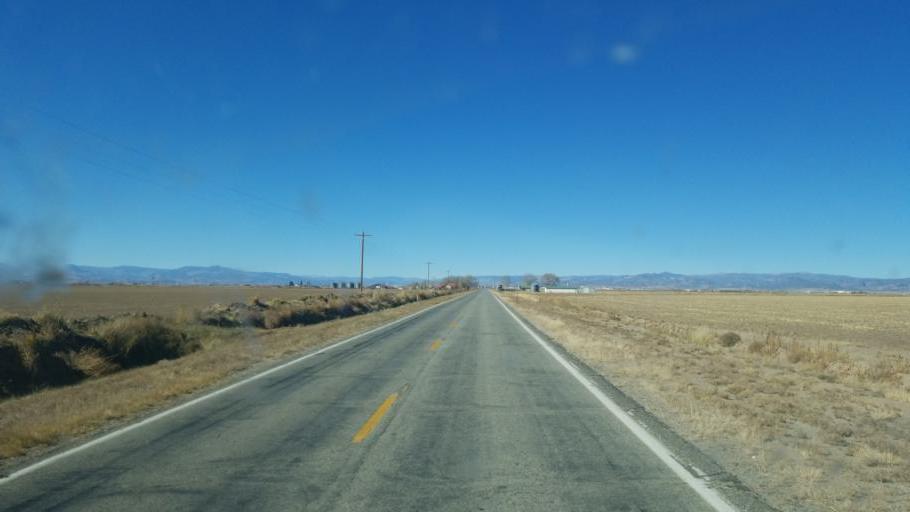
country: US
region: Colorado
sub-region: Saguache County
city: Center
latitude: 37.7483
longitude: -106.0411
